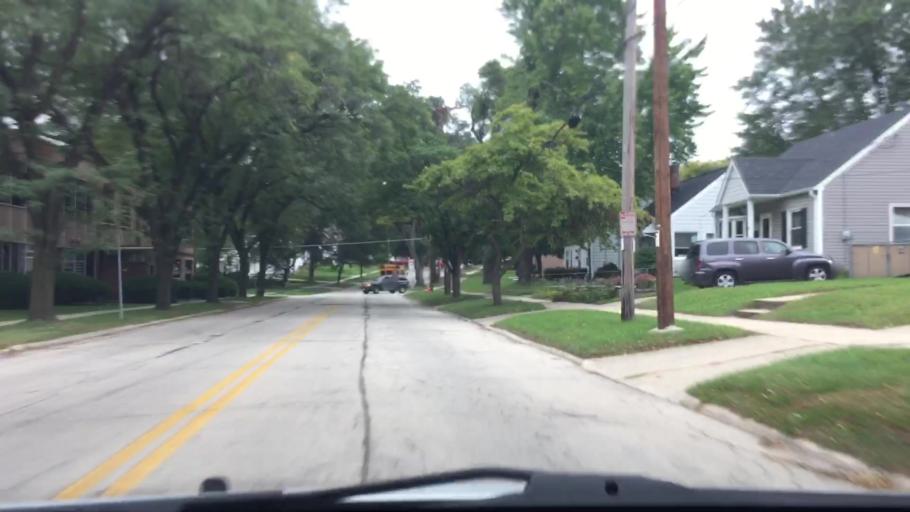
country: US
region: Wisconsin
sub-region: Waukesha County
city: Waukesha
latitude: 43.0165
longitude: -88.2132
